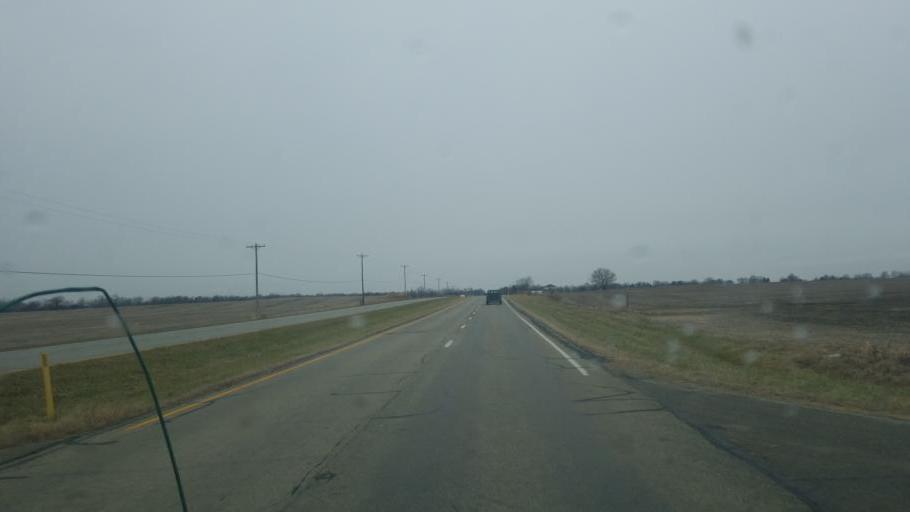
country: US
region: Indiana
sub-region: Hancock County
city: Greenfield
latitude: 39.7894
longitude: -85.6727
